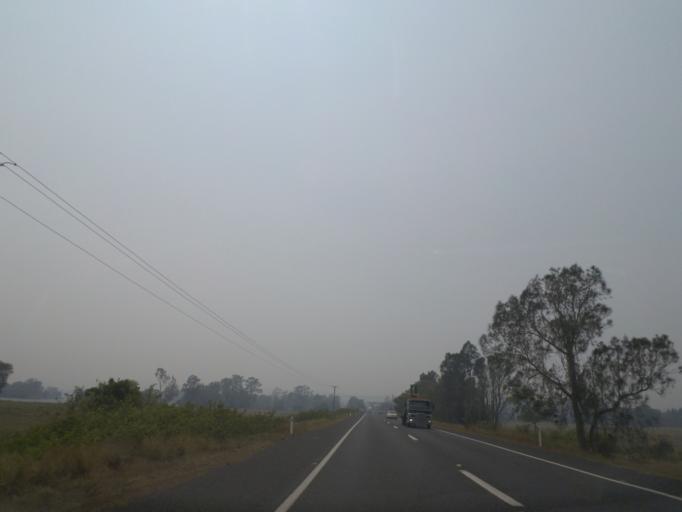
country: AU
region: New South Wales
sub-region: Clarence Valley
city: Maclean
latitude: -29.5659
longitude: 153.1256
